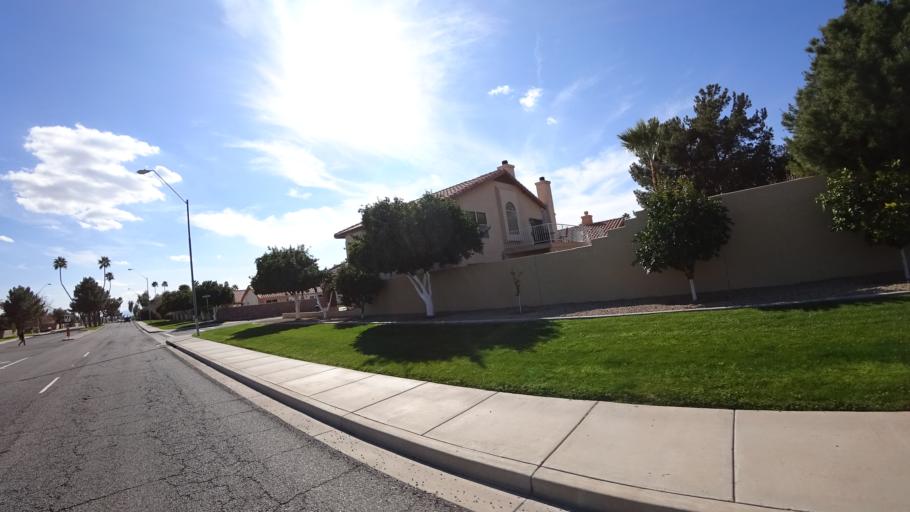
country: US
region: Arizona
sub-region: Maricopa County
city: Peoria
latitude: 33.6565
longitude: -112.2205
